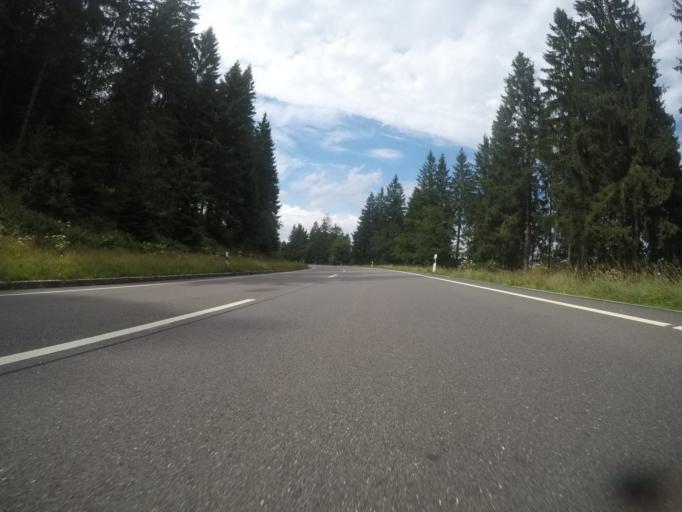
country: DE
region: Baden-Wuerttemberg
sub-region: Freiburg Region
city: Bad Peterstal-Griesbach
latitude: 48.4970
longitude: 8.2426
